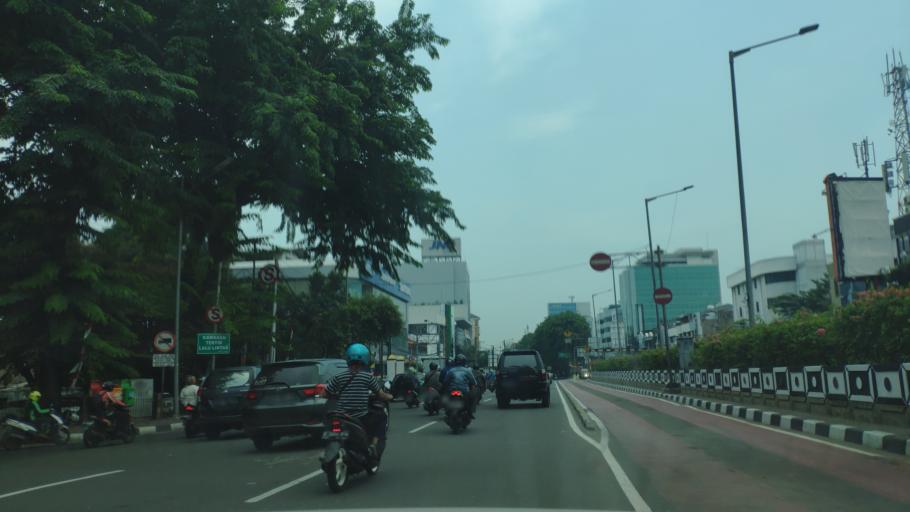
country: ID
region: Jakarta Raya
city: Jakarta
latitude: -6.1792
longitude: 106.7964
